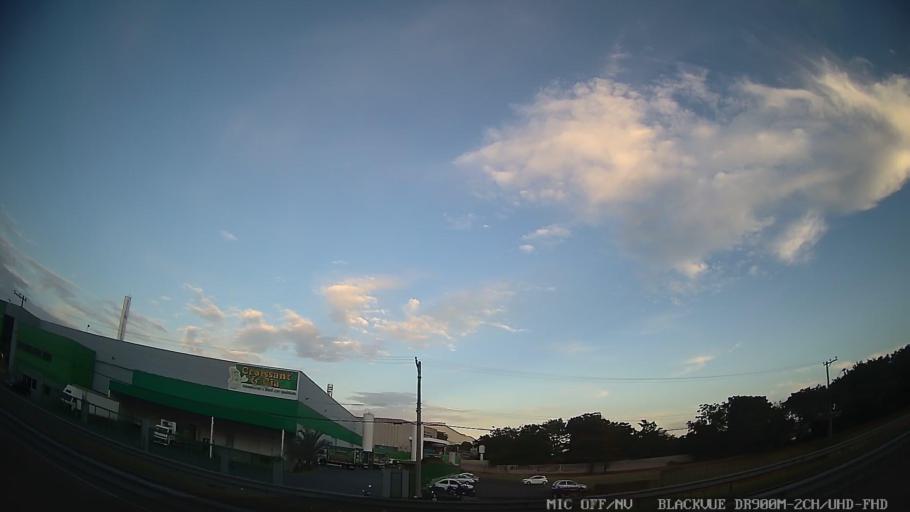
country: BR
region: Sao Paulo
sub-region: Indaiatuba
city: Indaiatuba
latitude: -23.1355
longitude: -47.2397
